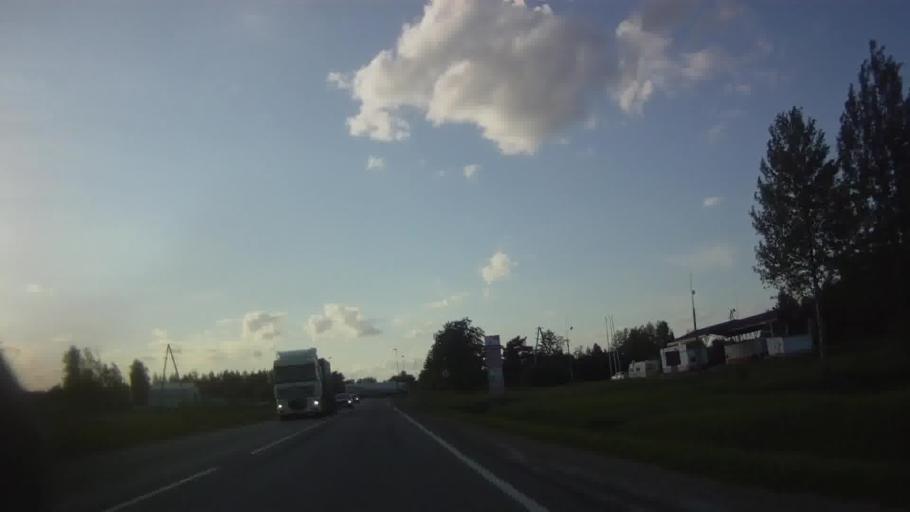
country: LV
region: Rezekne
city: Rezekne
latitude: 56.5389
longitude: 27.3018
